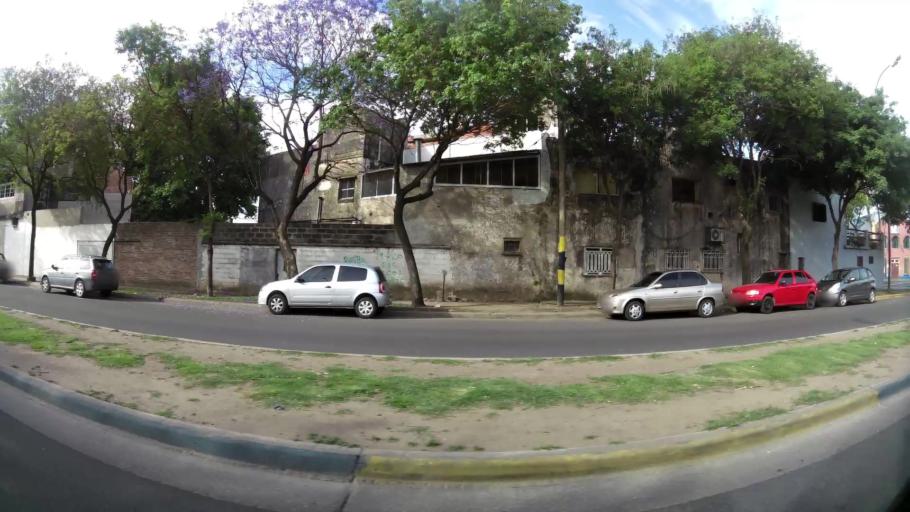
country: AR
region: Santa Fe
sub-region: Departamento de Rosario
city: Rosario
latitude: -32.9298
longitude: -60.6745
